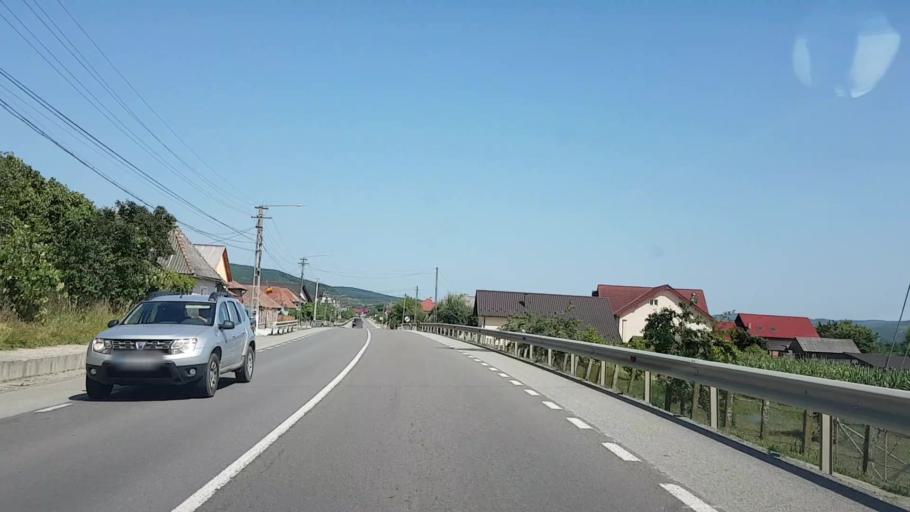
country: RO
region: Bistrita-Nasaud
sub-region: Comuna Uriu
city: Cristestii Ciceului
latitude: 47.1894
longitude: 24.1042
